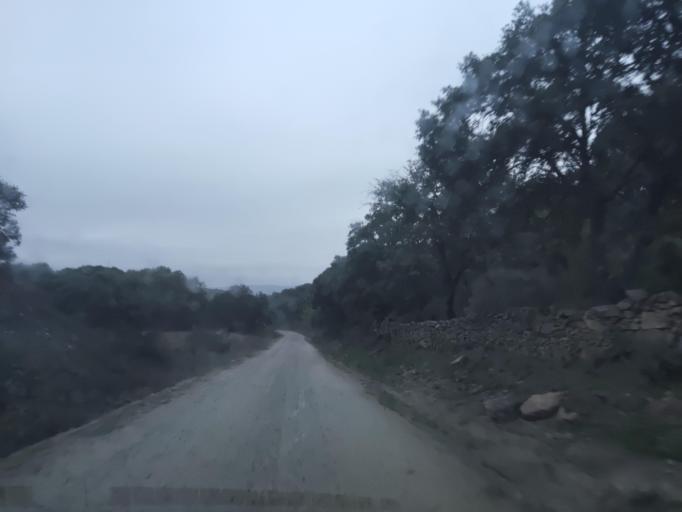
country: ES
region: Castille and Leon
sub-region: Provincia de Salamanca
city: Hinojosa de Duero
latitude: 40.9805
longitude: -6.8395
